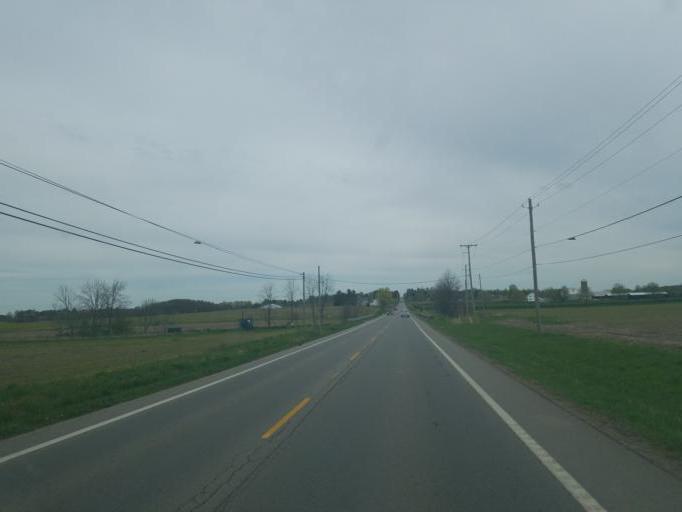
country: US
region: Ohio
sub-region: Wayne County
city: Orrville
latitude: 40.8712
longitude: -81.7634
